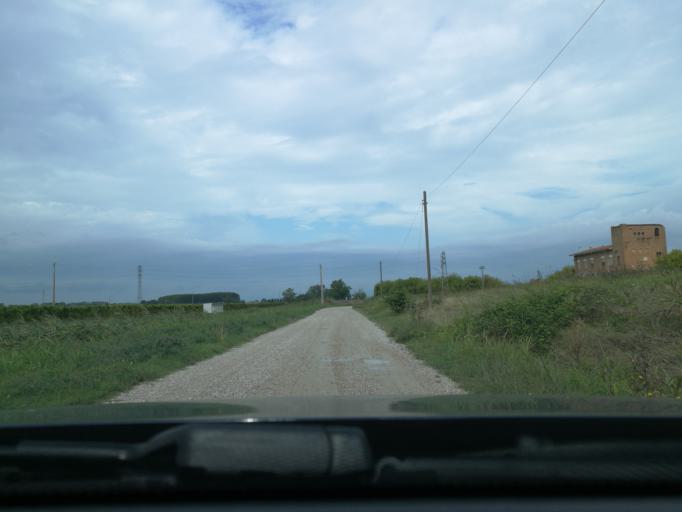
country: IT
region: Friuli Venezia Giulia
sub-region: Provincia di Udine
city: Pertegada
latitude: 45.7134
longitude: 13.0661
